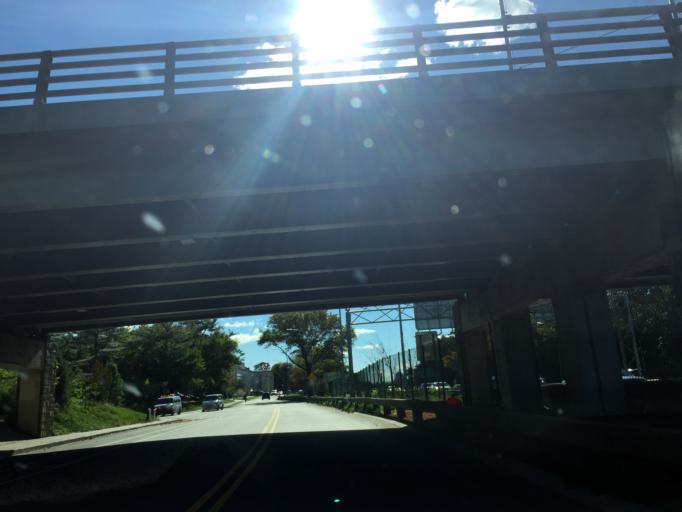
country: US
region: New York
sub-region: Queens County
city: Borough of Queens
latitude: 40.7476
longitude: -73.8485
